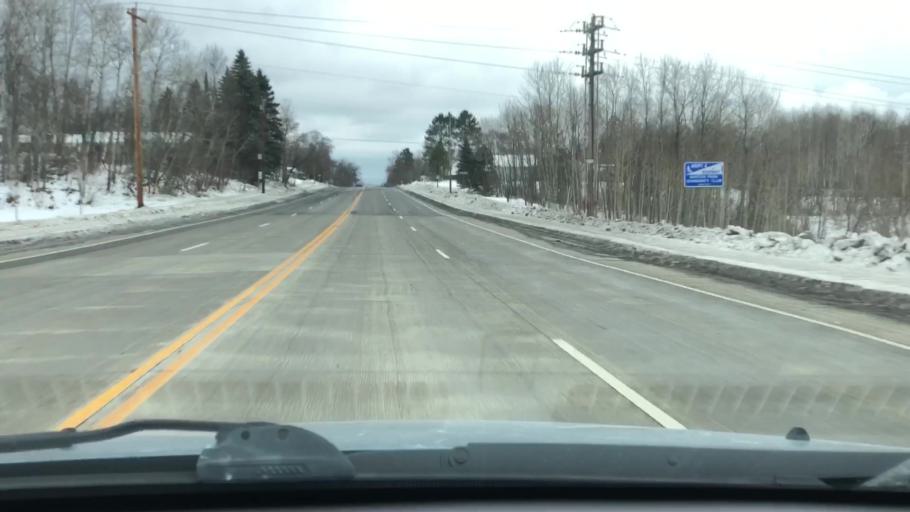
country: US
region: Minnesota
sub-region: Saint Louis County
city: Proctor
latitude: 46.7168
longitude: -92.2005
